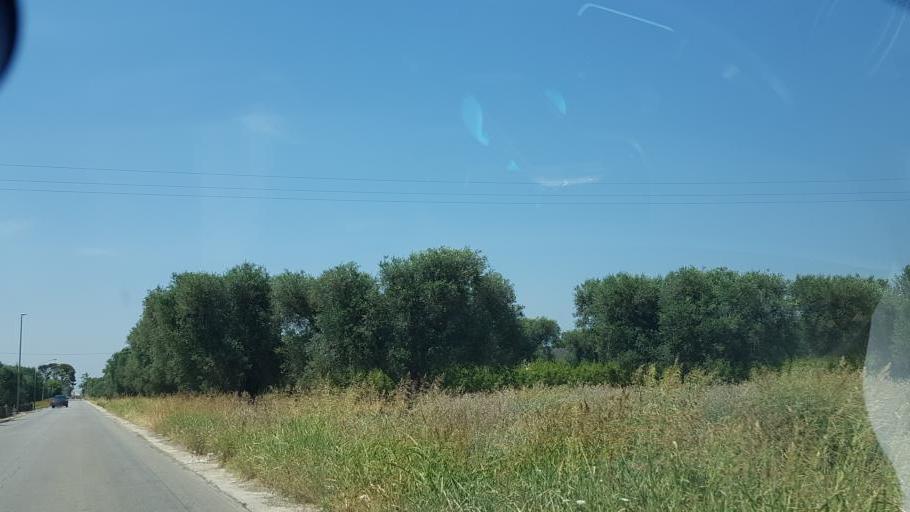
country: IT
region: Apulia
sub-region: Provincia di Brindisi
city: Mesagne
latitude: 40.5467
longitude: 17.8204
